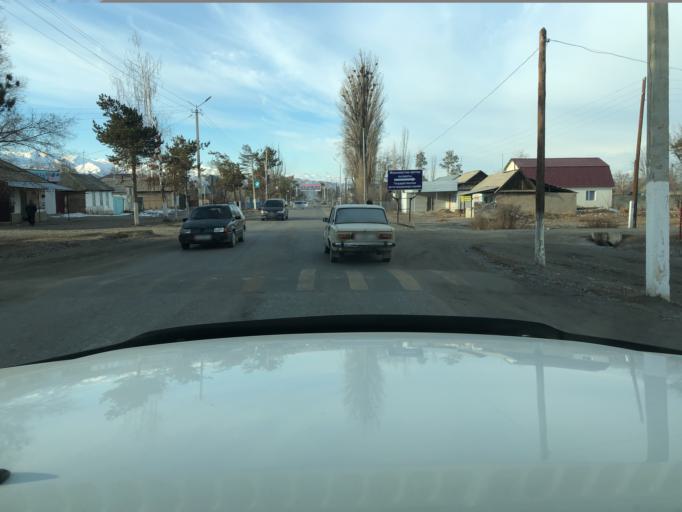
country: KG
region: Ysyk-Koel
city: Pokrovka
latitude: 42.3437
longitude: 78.0084
